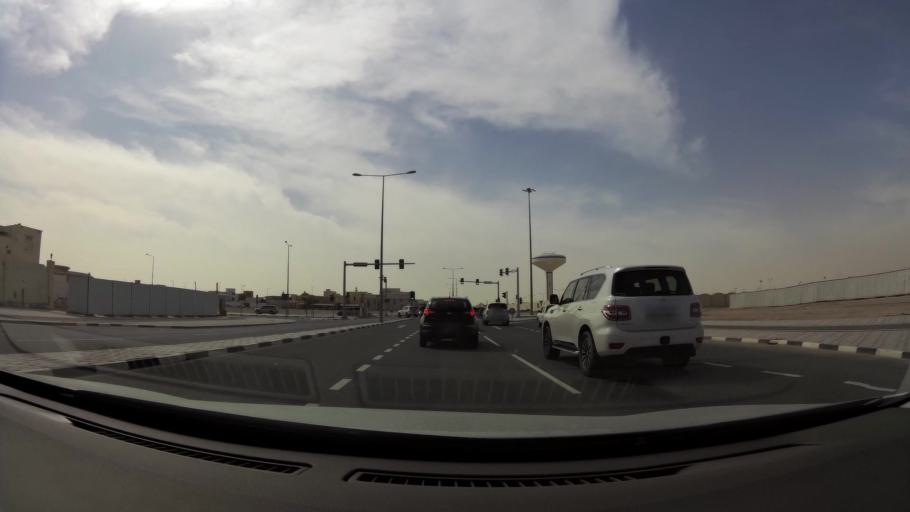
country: QA
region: Baladiyat ar Rayyan
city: Ar Rayyan
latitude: 25.3192
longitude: 51.4065
